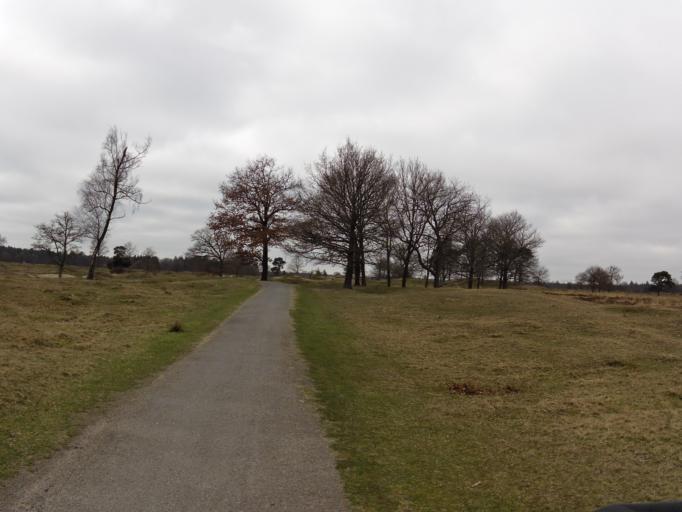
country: NL
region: Drenthe
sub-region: Gemeente Westerveld
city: Dwingeloo
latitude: 52.9245
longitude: 6.2942
